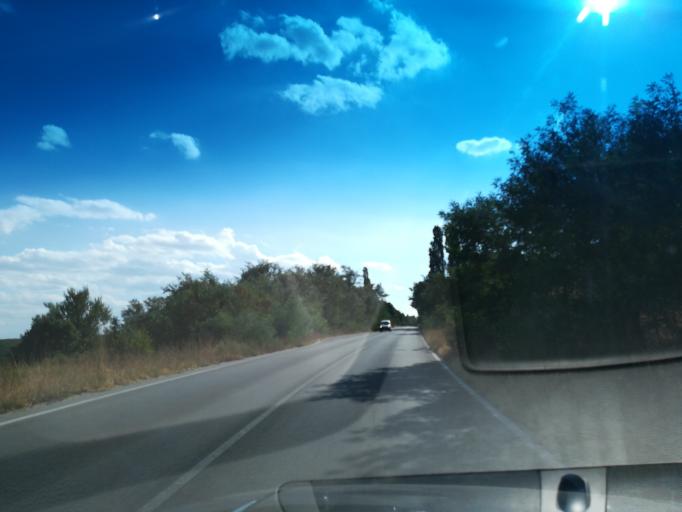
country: BG
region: Khaskovo
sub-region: Obshtina Mineralni Bani
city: Mineralni Bani
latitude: 42.0108
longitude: 25.3962
